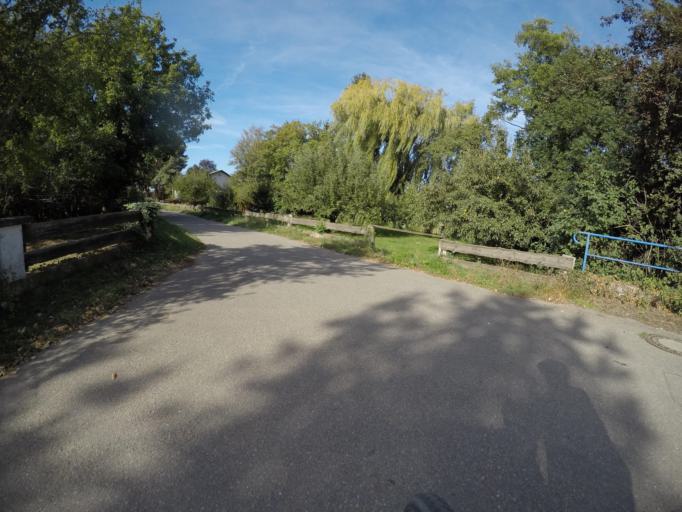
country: DE
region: Baden-Wuerttemberg
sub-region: Karlsruhe Region
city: Reilingen
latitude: 49.2910
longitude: 8.5794
